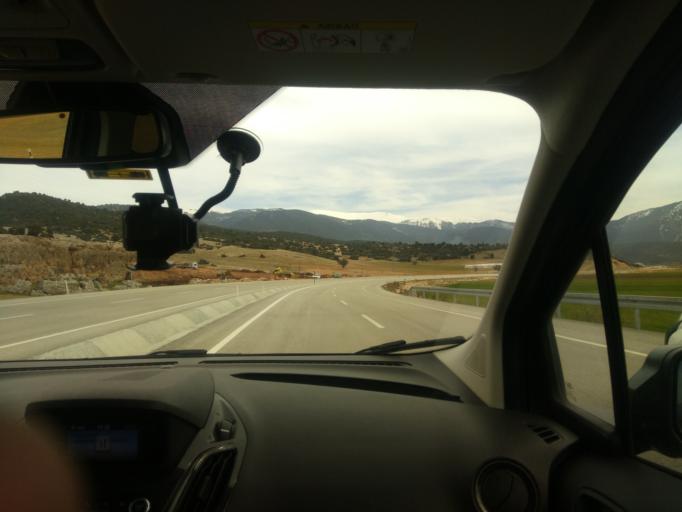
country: TR
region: Antalya
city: Elmali
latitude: 36.6334
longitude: 29.9386
